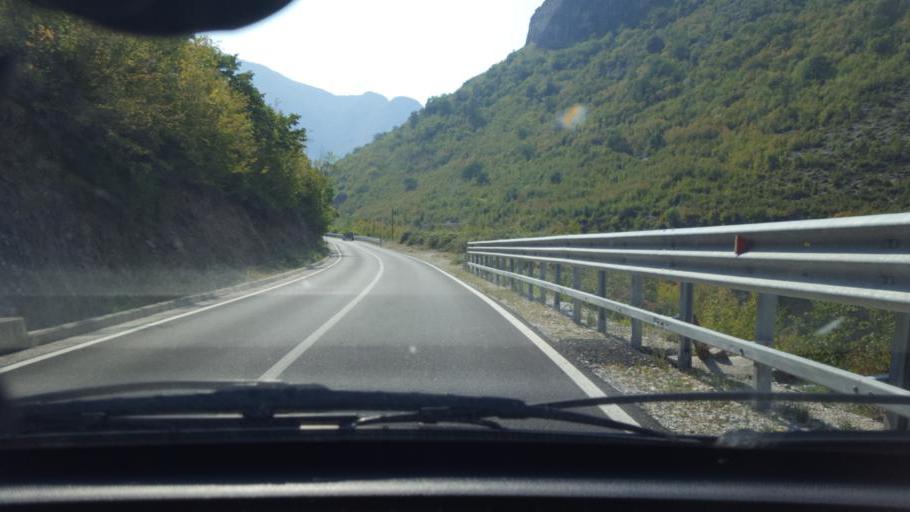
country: AL
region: Shkoder
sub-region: Rrethi i Malesia e Madhe
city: Kastrat
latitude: 42.4427
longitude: 19.5397
